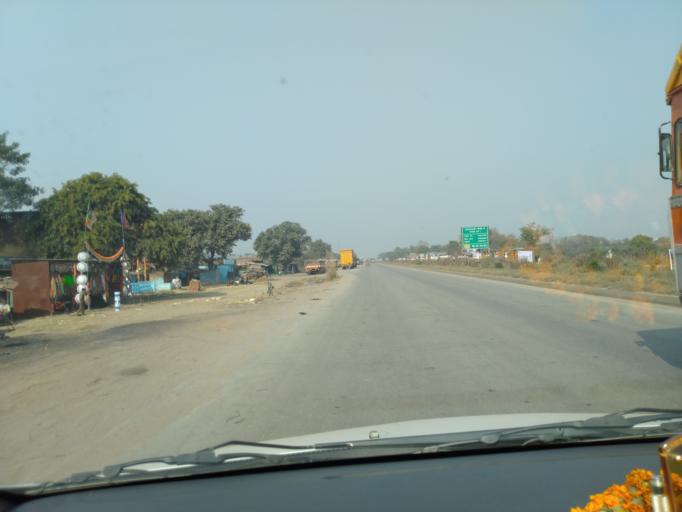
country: IN
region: Bihar
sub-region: Aurangabad
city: Aurangabad
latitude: 24.7992
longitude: 84.3097
